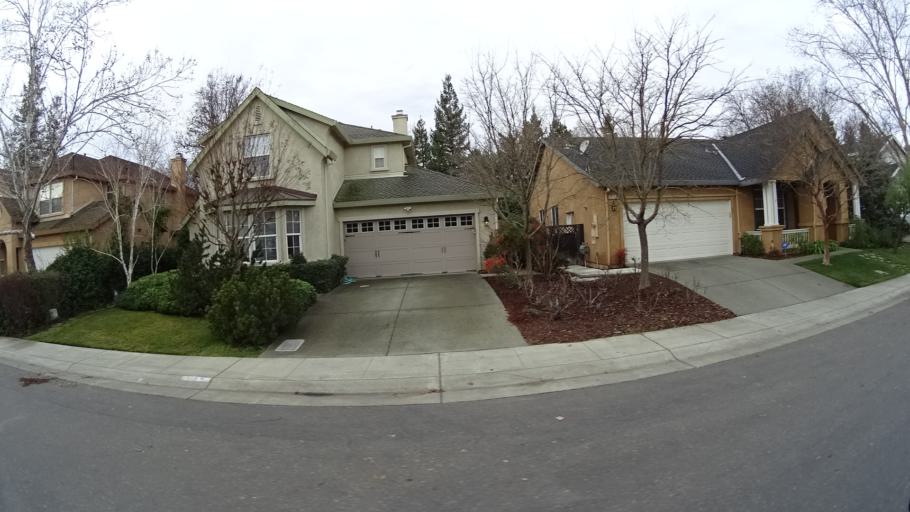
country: US
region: California
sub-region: Yolo County
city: Davis
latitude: 38.5702
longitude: -121.7258
